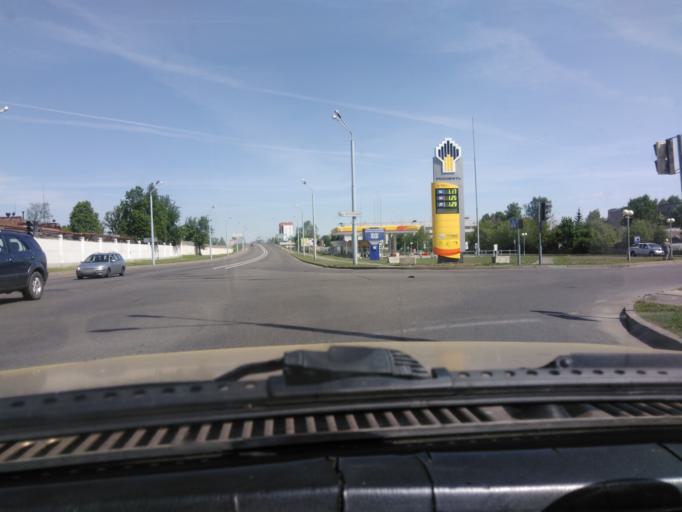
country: BY
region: Mogilev
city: Mahilyow
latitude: 53.9157
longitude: 30.3479
